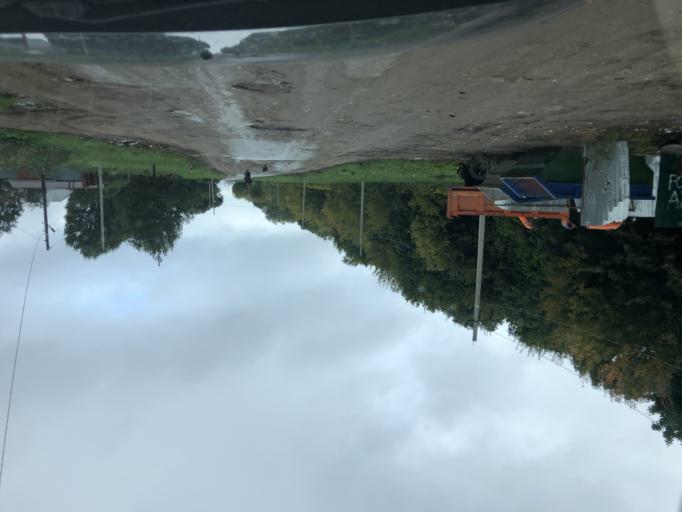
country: RU
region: Tula
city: Mendeleyevskiy
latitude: 54.1745
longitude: 37.5518
